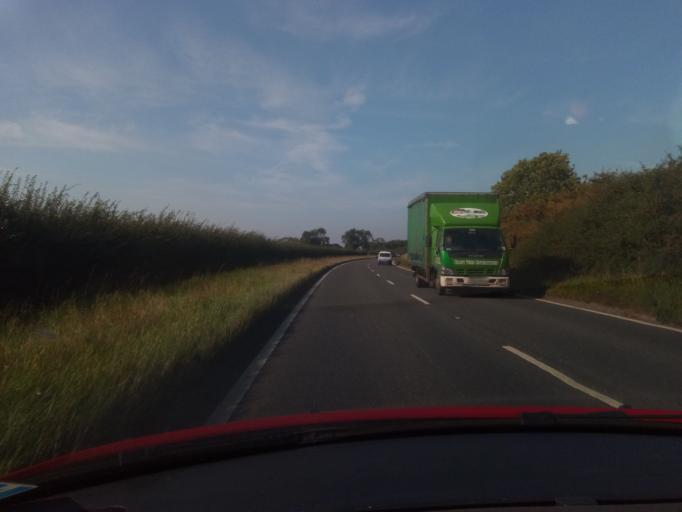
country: GB
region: England
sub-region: City of York
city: Skelton
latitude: 54.0185
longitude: -1.1572
